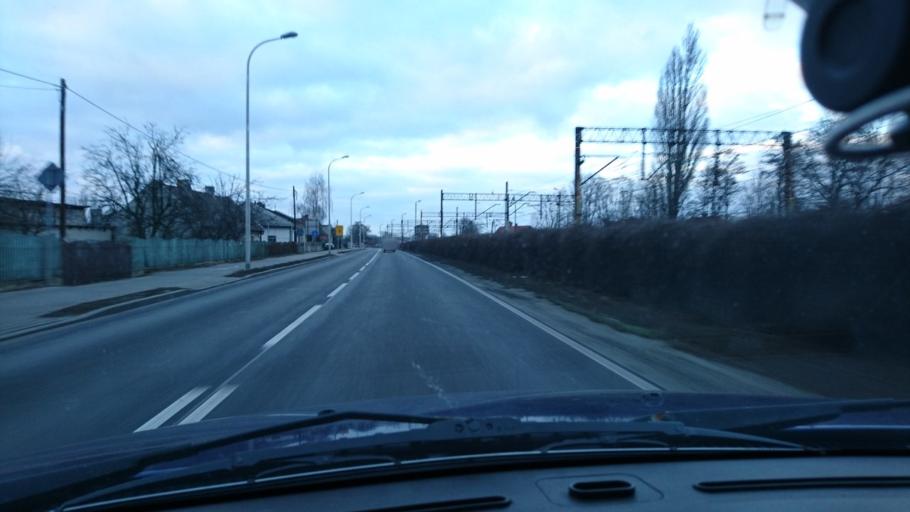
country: PL
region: Greater Poland Voivodeship
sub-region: Powiat kepinski
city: Kepno
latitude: 51.2991
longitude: 17.9965
